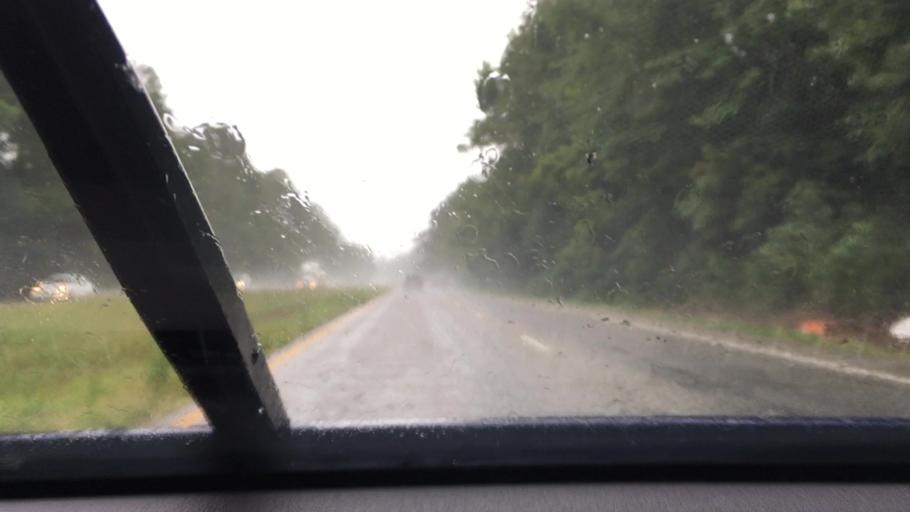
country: US
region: South Carolina
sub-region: Sumter County
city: Stateburg
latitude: 33.9477
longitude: -80.5425
